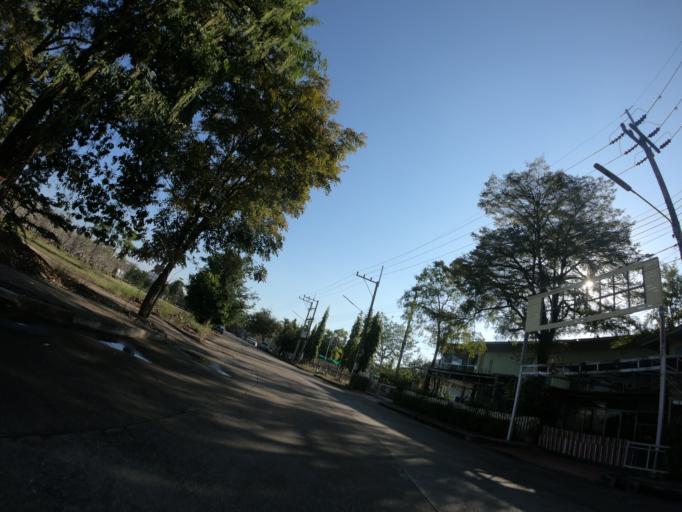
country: TH
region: Chiang Mai
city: Chiang Mai
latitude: 18.8044
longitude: 99.0238
